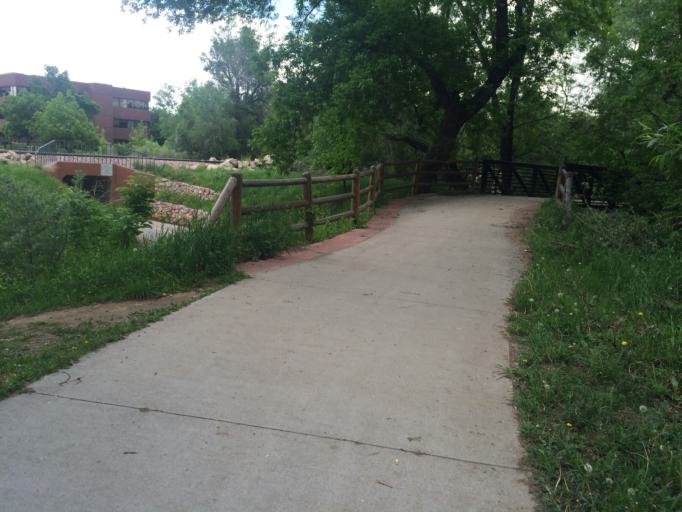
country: US
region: Colorado
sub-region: Boulder County
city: Boulder
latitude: 40.0193
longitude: -105.2362
